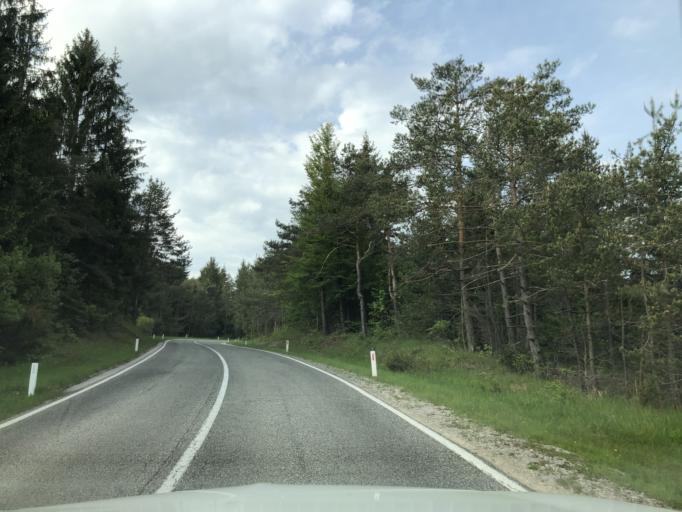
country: SI
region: Bloke
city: Nova Vas
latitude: 45.7709
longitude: 14.4838
